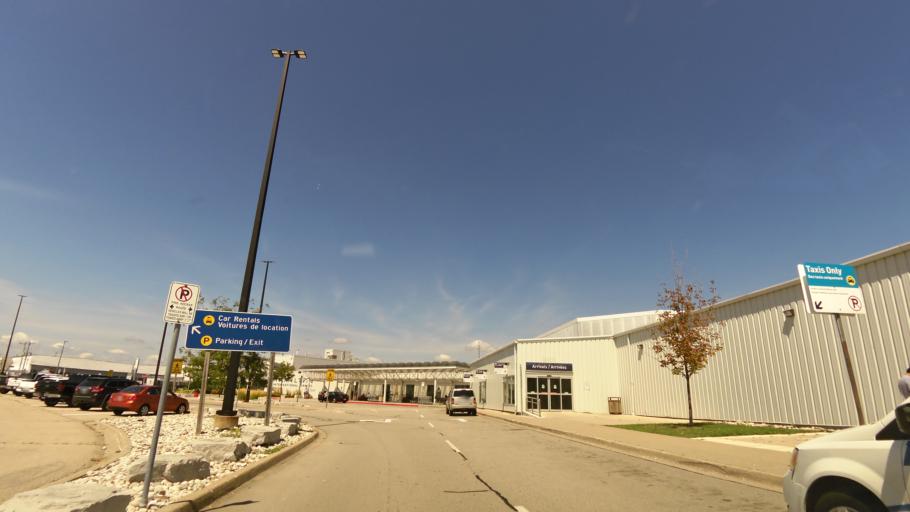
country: CA
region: Ontario
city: Ancaster
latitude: 43.1626
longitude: -79.9262
